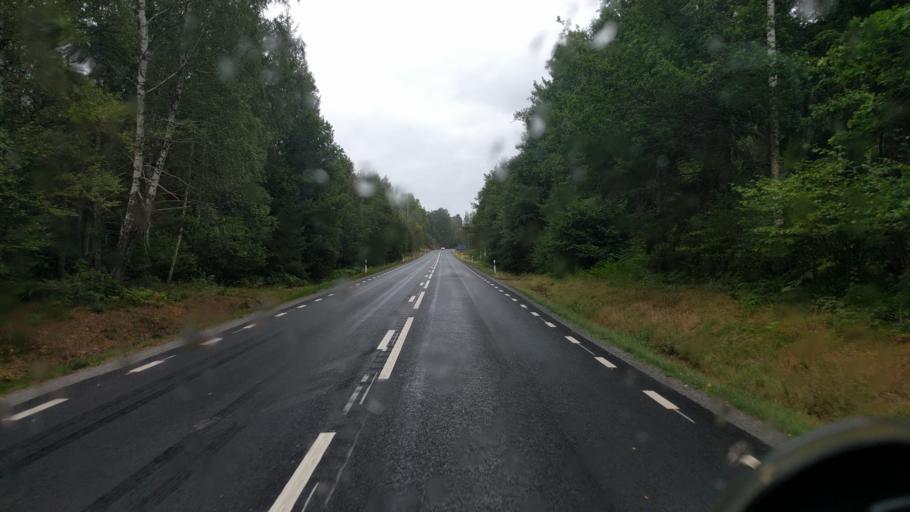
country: SE
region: Kalmar
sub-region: Vasterviks Kommun
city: Ankarsrum
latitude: 57.7223
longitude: 16.4414
